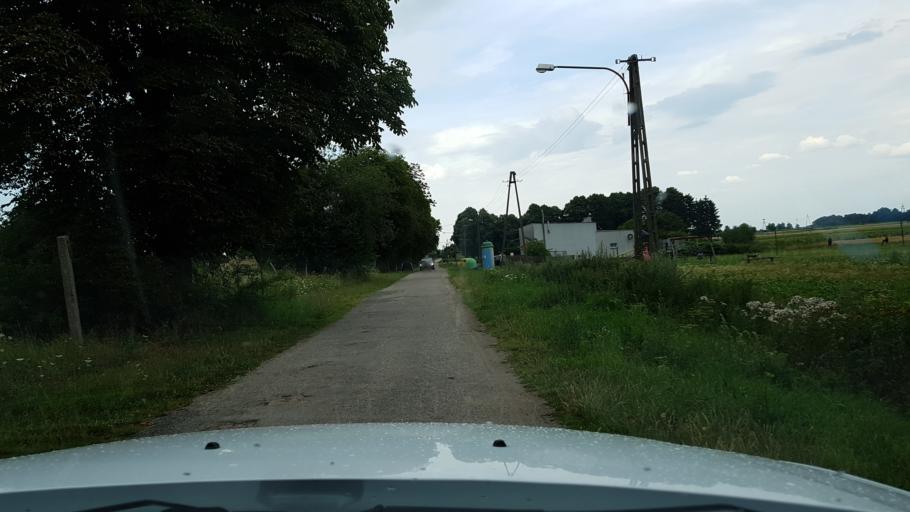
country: PL
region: West Pomeranian Voivodeship
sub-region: Powiat walecki
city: Walcz
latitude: 53.3509
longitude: 16.3589
